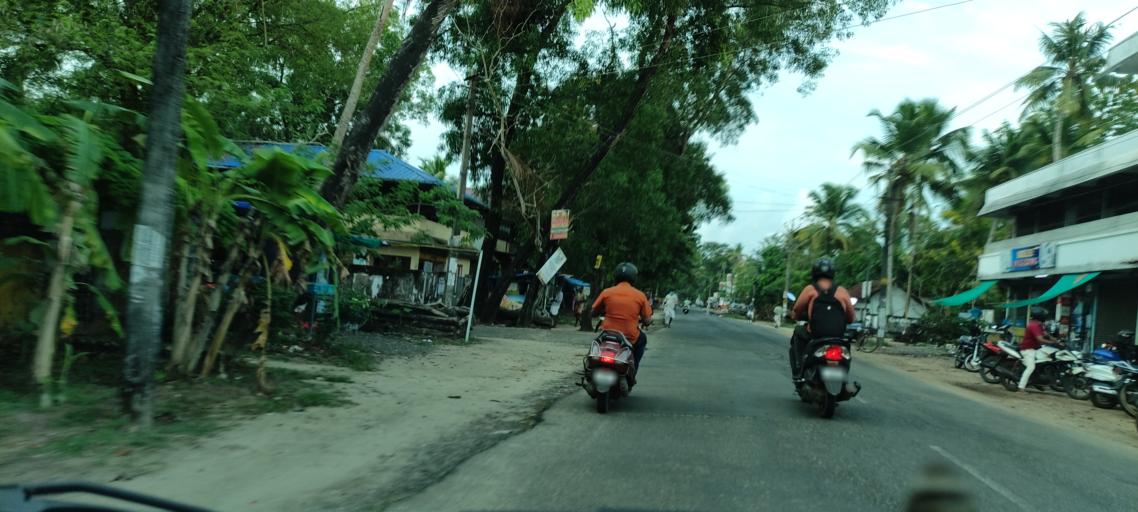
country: IN
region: Kerala
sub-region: Alappuzha
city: Kutiatodu
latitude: 9.8050
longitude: 76.3535
